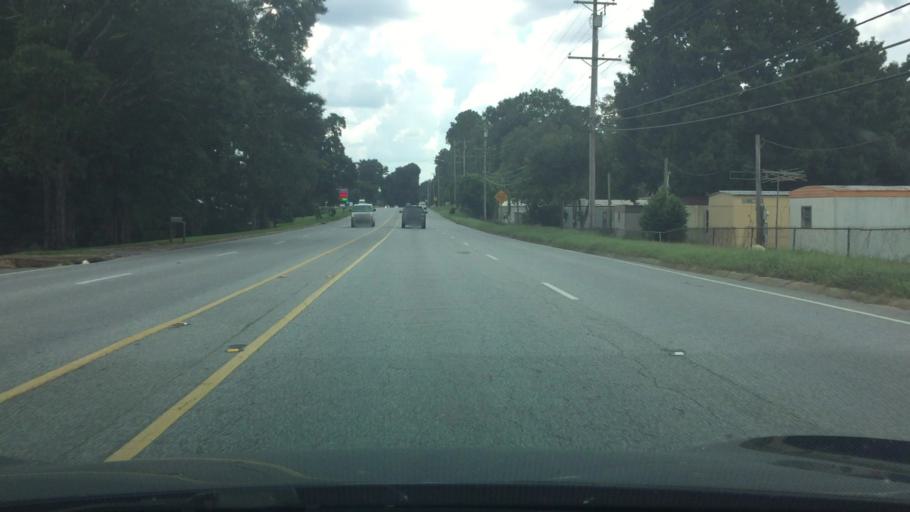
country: US
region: Alabama
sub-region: Pike County
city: Troy
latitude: 31.7624
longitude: -85.9616
